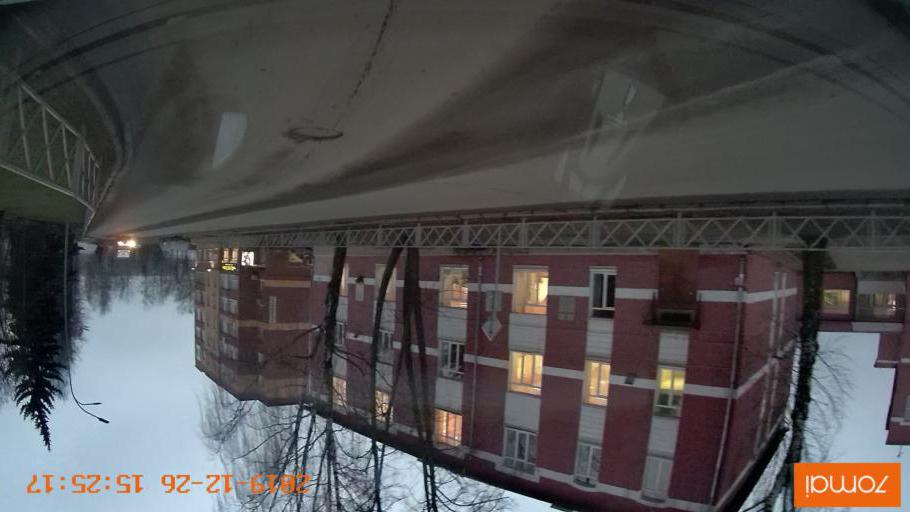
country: RU
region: Jaroslavl
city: Rybinsk
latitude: 58.0528
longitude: 38.8388
